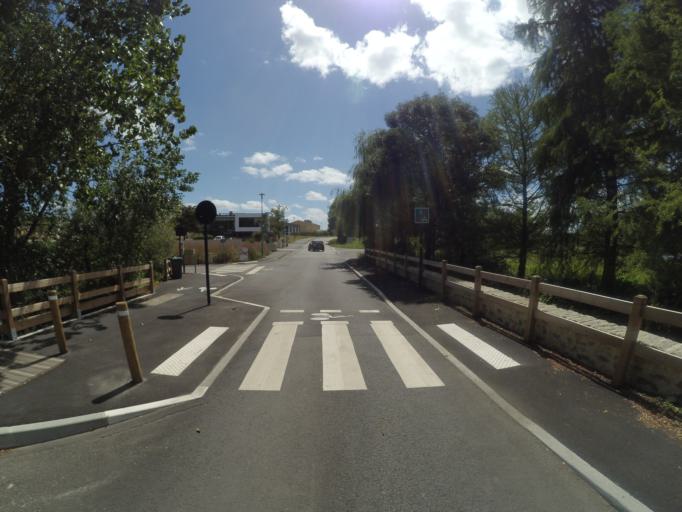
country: FR
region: Pays de la Loire
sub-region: Departement de la Loire-Atlantique
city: Aigrefeuille-sur-Maine
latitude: 47.0726
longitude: -1.4001
